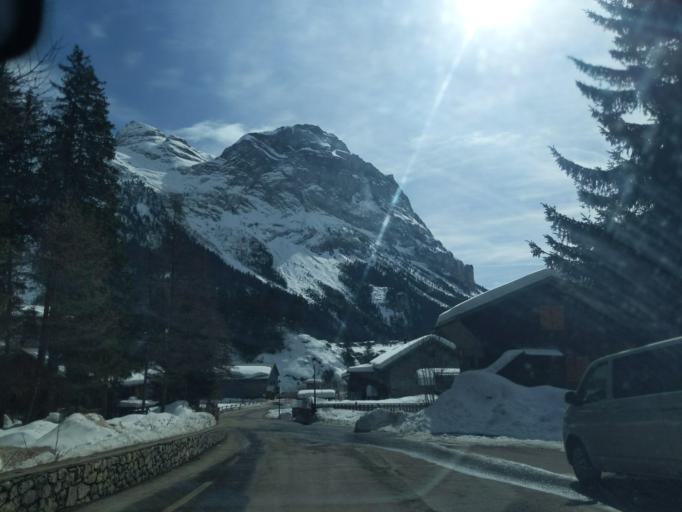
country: FR
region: Rhone-Alpes
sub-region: Departement de la Savoie
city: Courchevel
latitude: 45.3843
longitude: 6.7199
